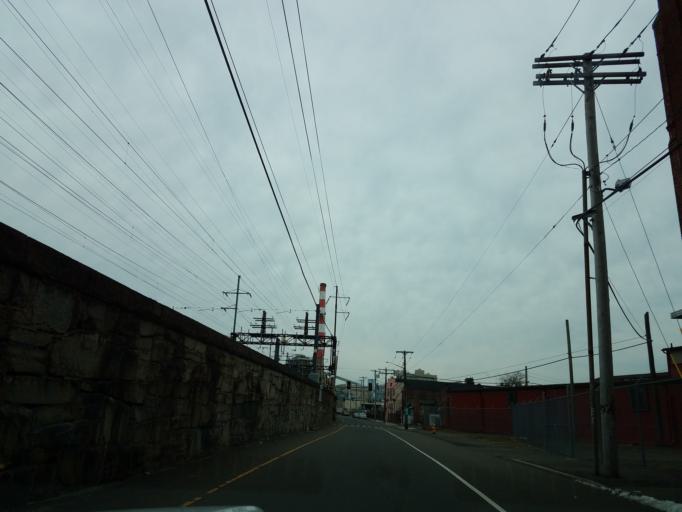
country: US
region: Connecticut
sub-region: Fairfield County
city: Bridgeport
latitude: 41.1695
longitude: -73.1917
